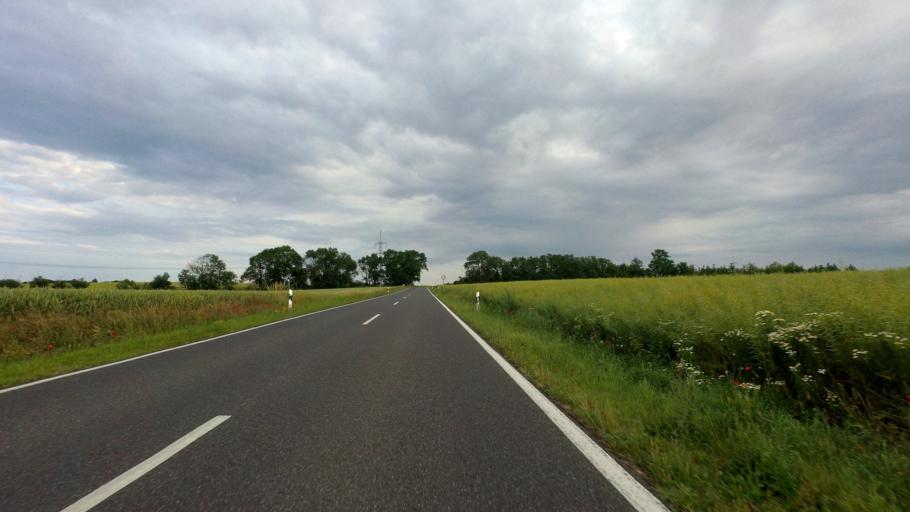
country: DE
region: Brandenburg
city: Pawesin
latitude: 52.5661
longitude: 12.7685
